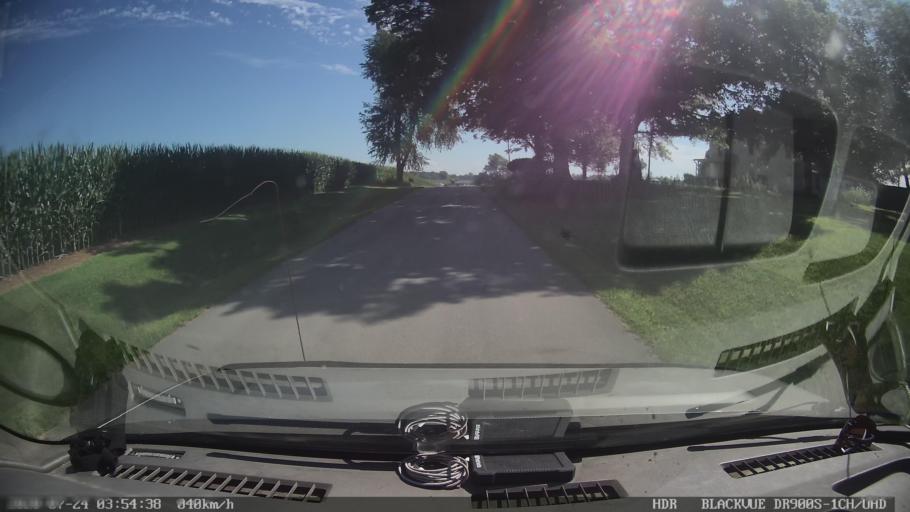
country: US
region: Kentucky
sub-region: Todd County
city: Elkton
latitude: 36.7789
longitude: -87.2338
